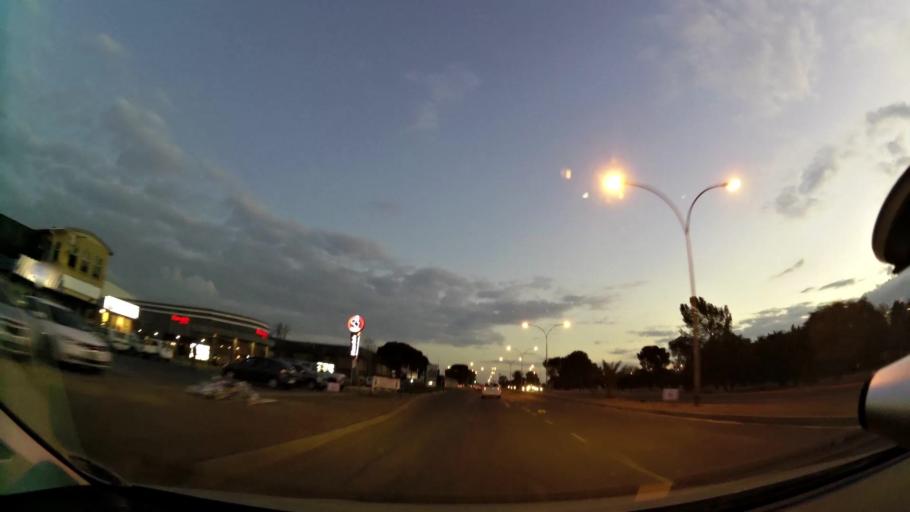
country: ZA
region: Orange Free State
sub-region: Mangaung Metropolitan Municipality
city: Bloemfontein
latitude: -29.1542
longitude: 26.1887
